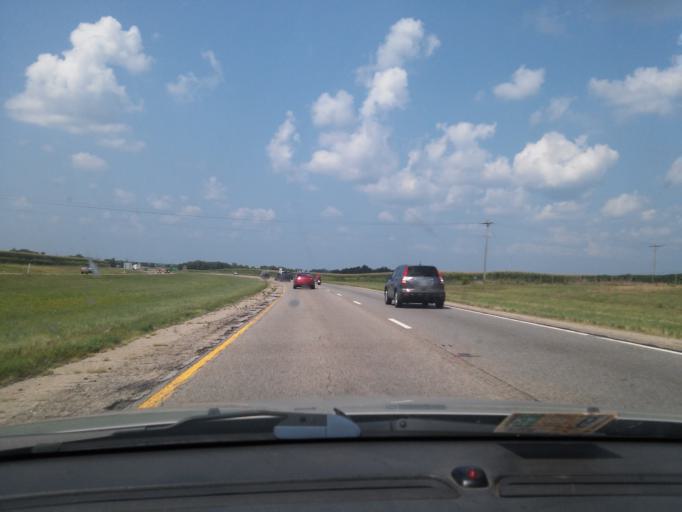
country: US
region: Illinois
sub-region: Logan County
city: Atlanta
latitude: 40.2663
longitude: -89.2137
